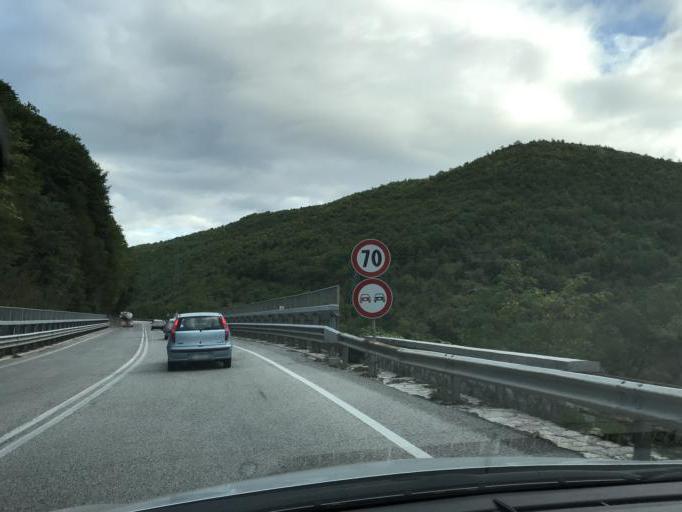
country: IT
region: Umbria
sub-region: Provincia di Perugia
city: Spoleto
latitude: 42.6813
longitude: 12.7269
